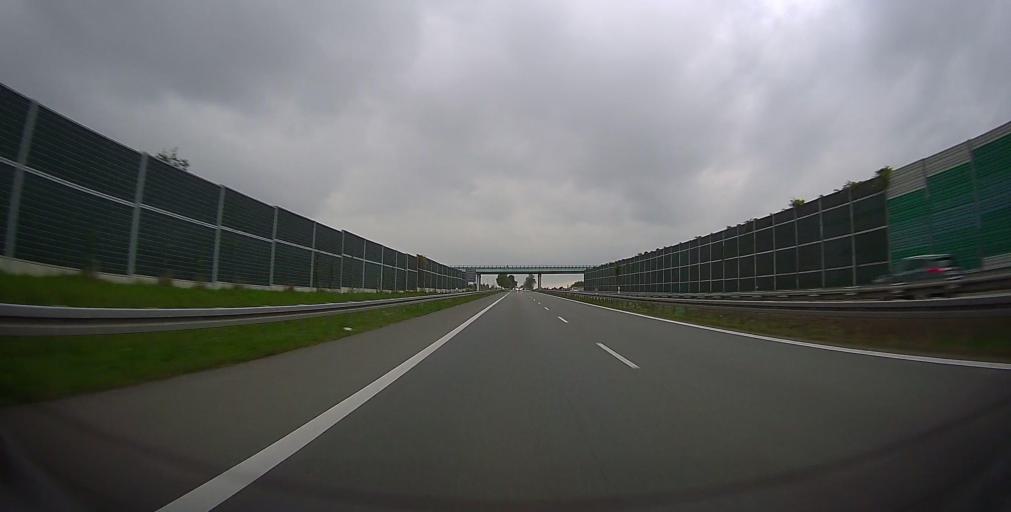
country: PL
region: Masovian Voivodeship
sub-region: Powiat bialobrzeski
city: Stara Blotnica
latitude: 51.5825
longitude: 21.0008
